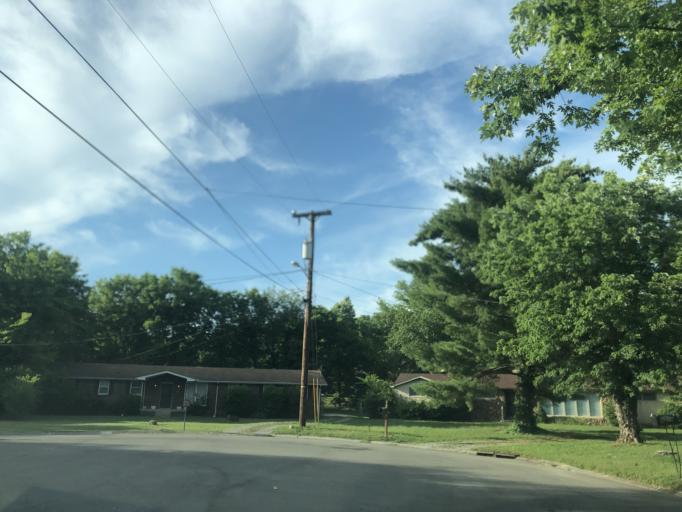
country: US
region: Tennessee
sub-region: Davidson County
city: Nashville
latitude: 36.2181
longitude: -86.8568
